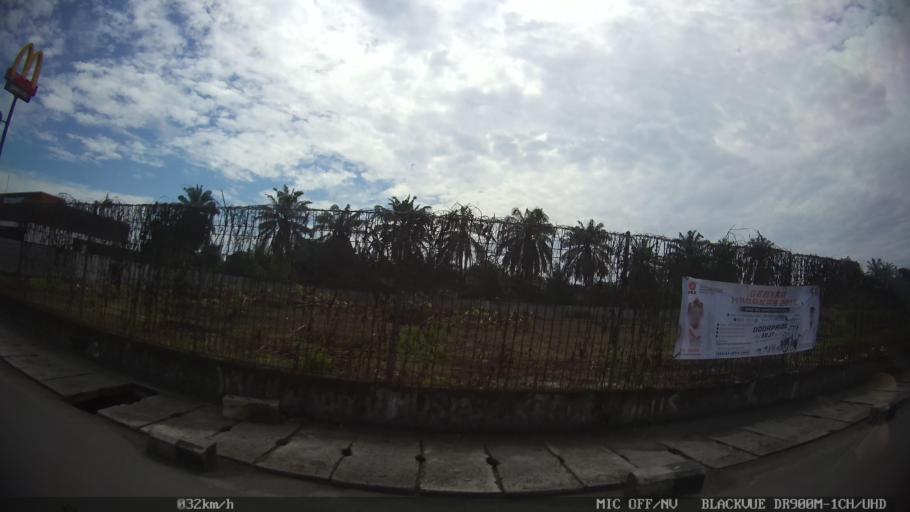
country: ID
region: North Sumatra
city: Medan
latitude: 3.6172
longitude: 98.7073
